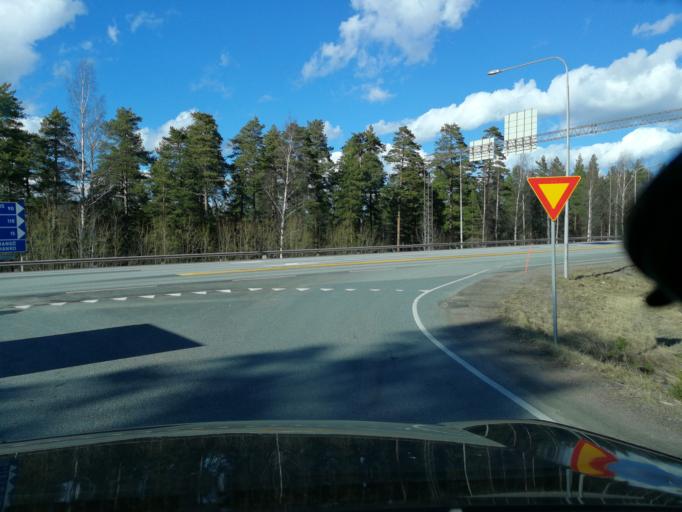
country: FI
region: Uusimaa
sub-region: Raaseporin
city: Ekenaes
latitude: 59.9879
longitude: 23.4821
